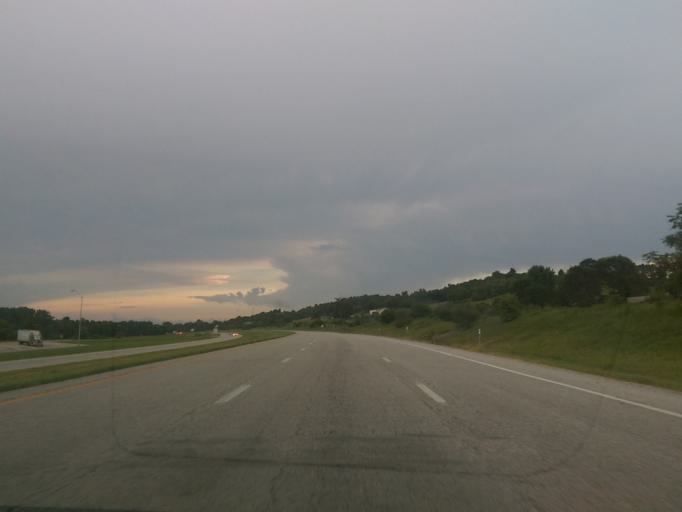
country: US
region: Missouri
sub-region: Holt County
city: Mound City
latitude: 40.1027
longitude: -95.2143
